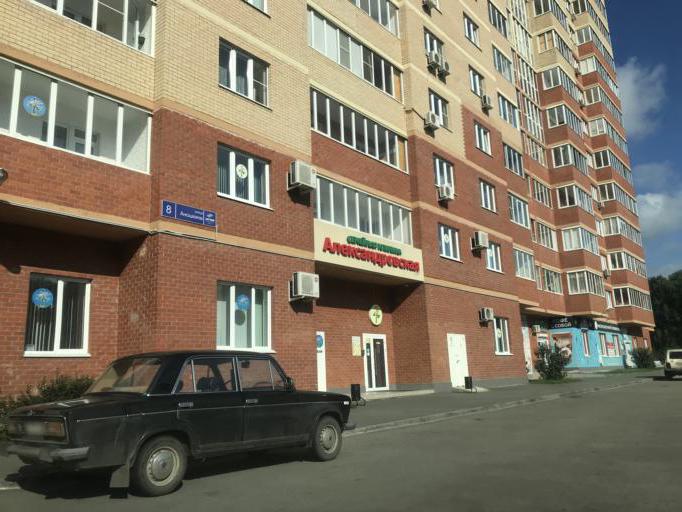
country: RU
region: Chelyabinsk
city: Roshchino
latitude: 55.1944
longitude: 61.2852
